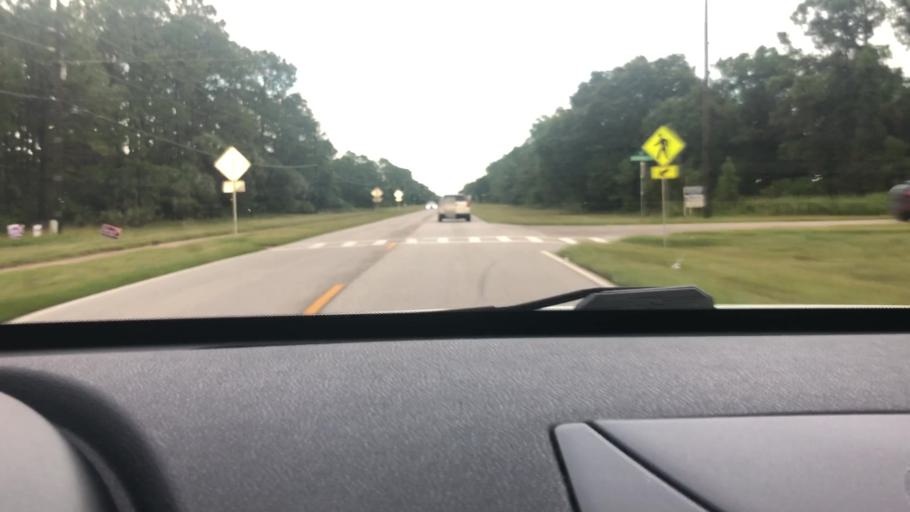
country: US
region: Florida
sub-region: Charlotte County
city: Port Charlotte
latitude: 27.0690
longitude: -82.1342
